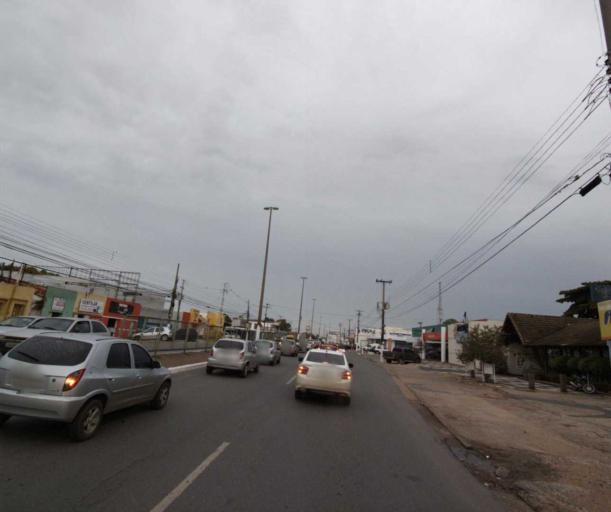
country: BR
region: Mato Grosso
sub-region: Cuiaba
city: Cuiaba
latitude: -15.6278
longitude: -56.0567
